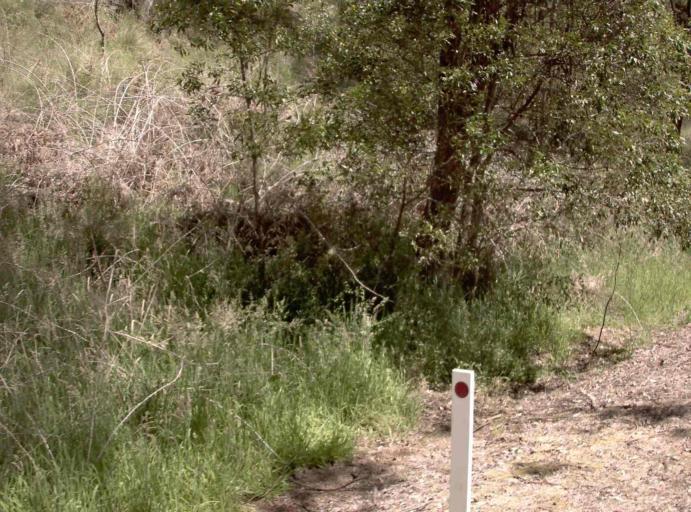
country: AU
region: Victoria
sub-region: East Gippsland
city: Lakes Entrance
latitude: -37.2280
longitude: 148.2632
